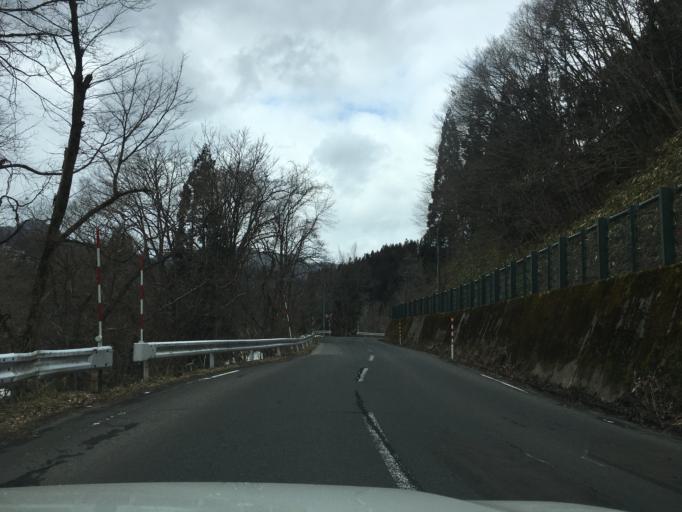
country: JP
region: Akita
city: Odate
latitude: 40.4377
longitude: 140.6396
